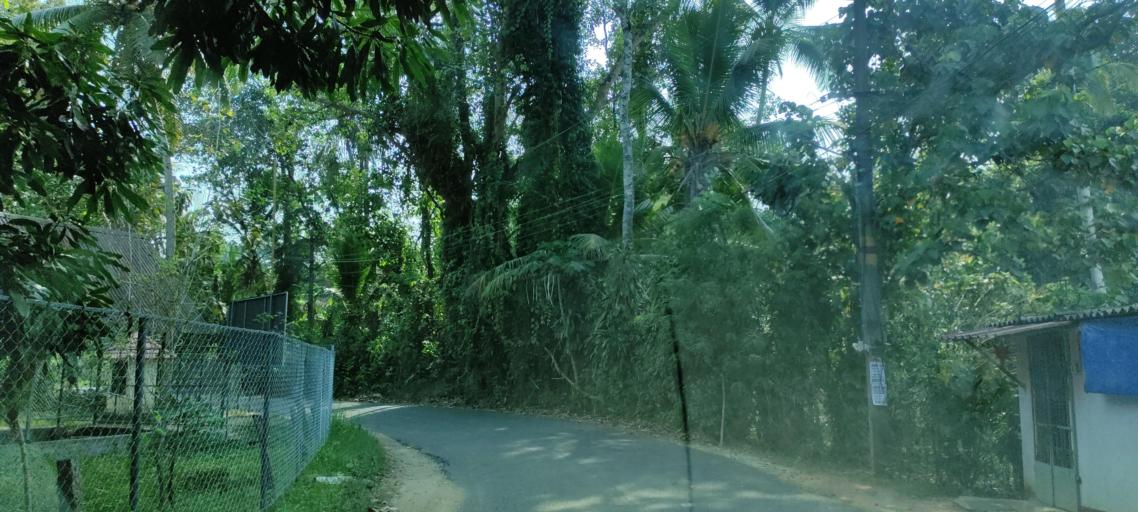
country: IN
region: Kerala
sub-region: Pattanamtitta
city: Tiruvalla
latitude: 9.3459
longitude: 76.5434
